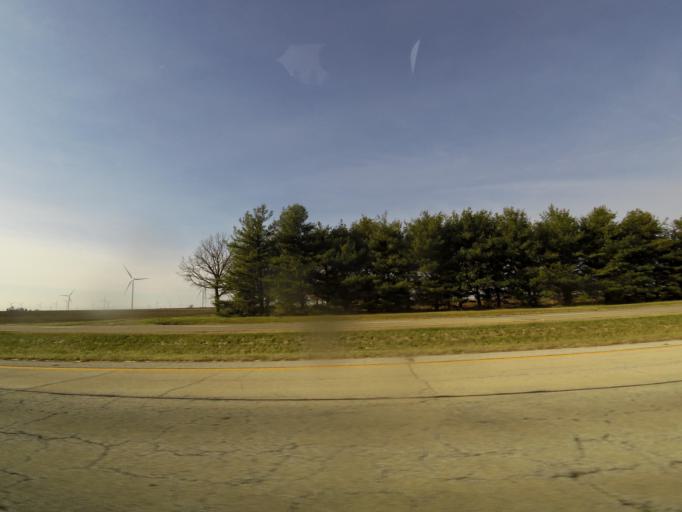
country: US
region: Illinois
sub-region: Macon County
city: Maroa
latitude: 40.0070
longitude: -88.9562
